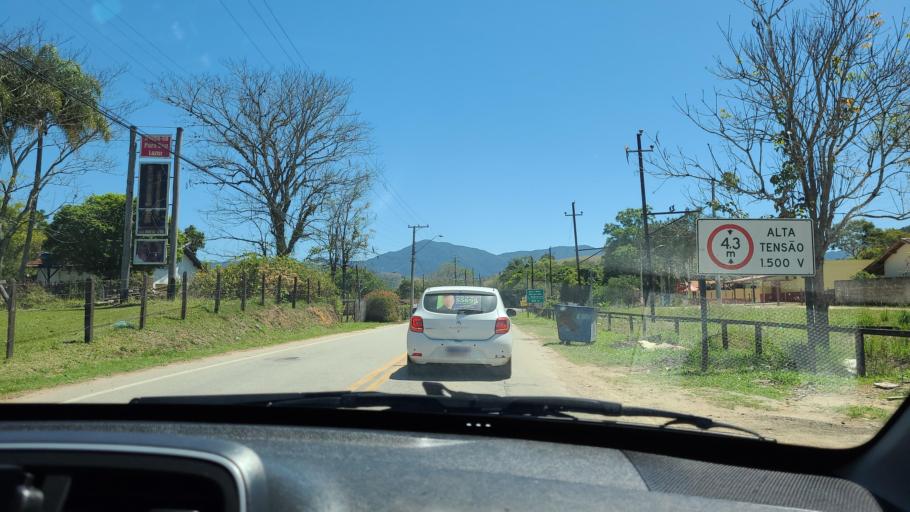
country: BR
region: Sao Paulo
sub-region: Tremembe
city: Tremembe
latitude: -22.8876
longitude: -45.5494
